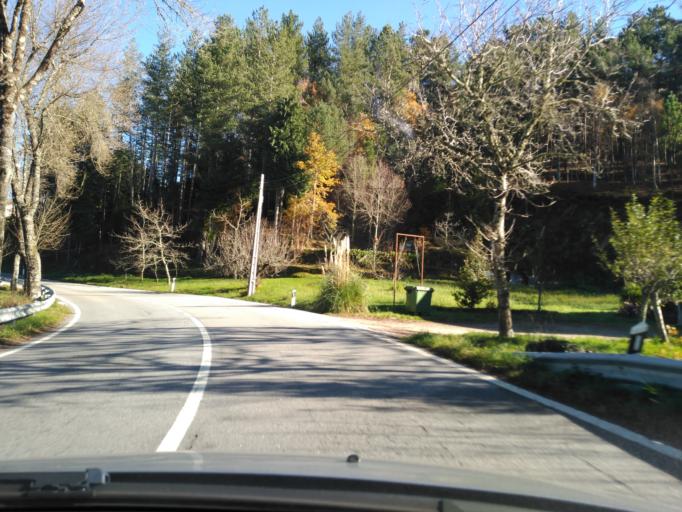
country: PT
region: Braga
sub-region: Cabeceiras de Basto
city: Cabeceiras de Basto
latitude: 41.6709
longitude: -7.9640
